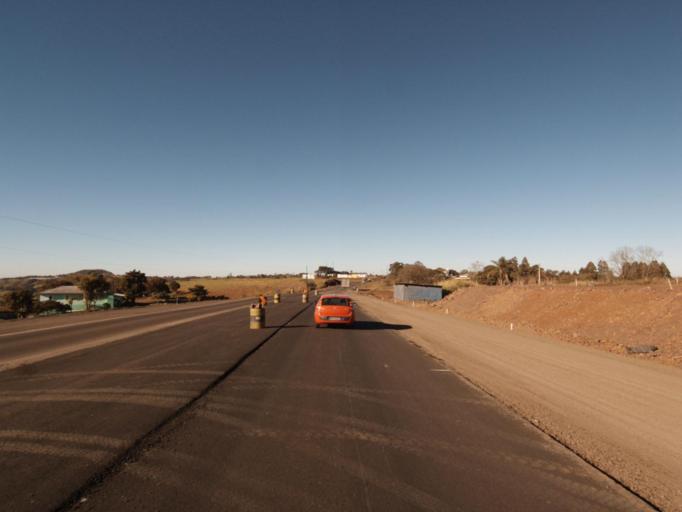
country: AR
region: Misiones
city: Bernardo de Irigoyen
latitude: -26.6388
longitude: -53.5185
